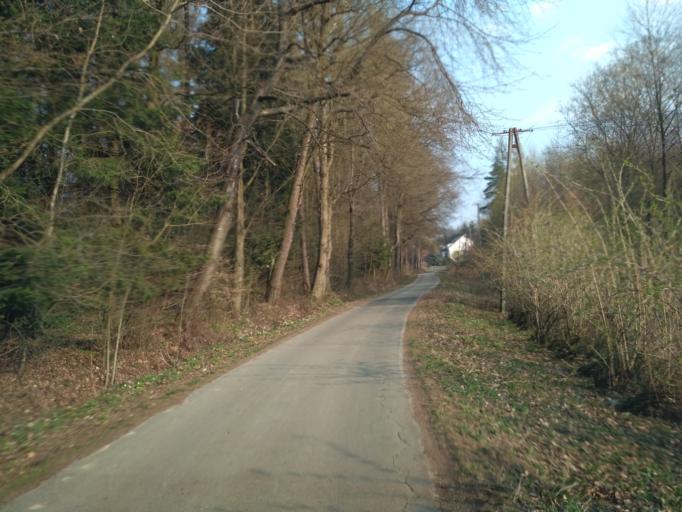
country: PL
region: Subcarpathian Voivodeship
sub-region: Powiat strzyzowski
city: Wisniowa
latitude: 49.8821
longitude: 21.6350
